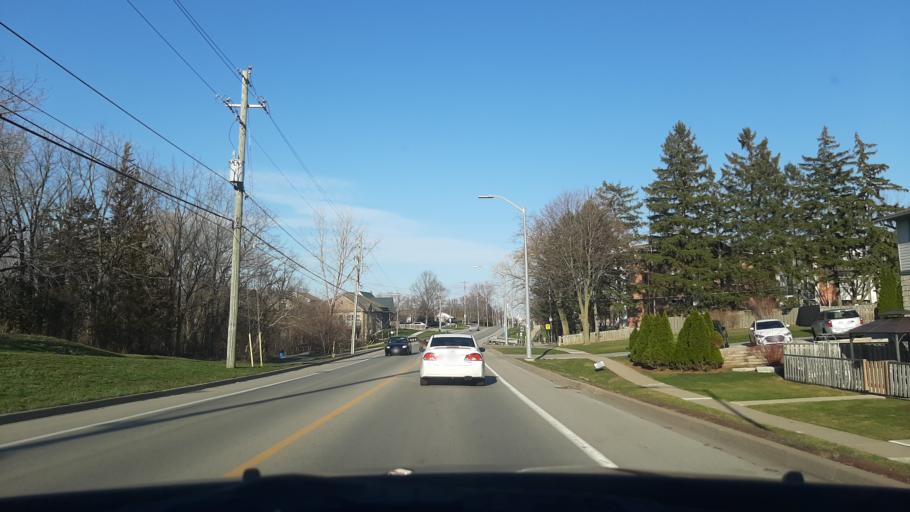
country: CA
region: Ontario
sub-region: Regional Municipality of Niagara
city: St. Catharines
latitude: 43.2122
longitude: -79.2272
